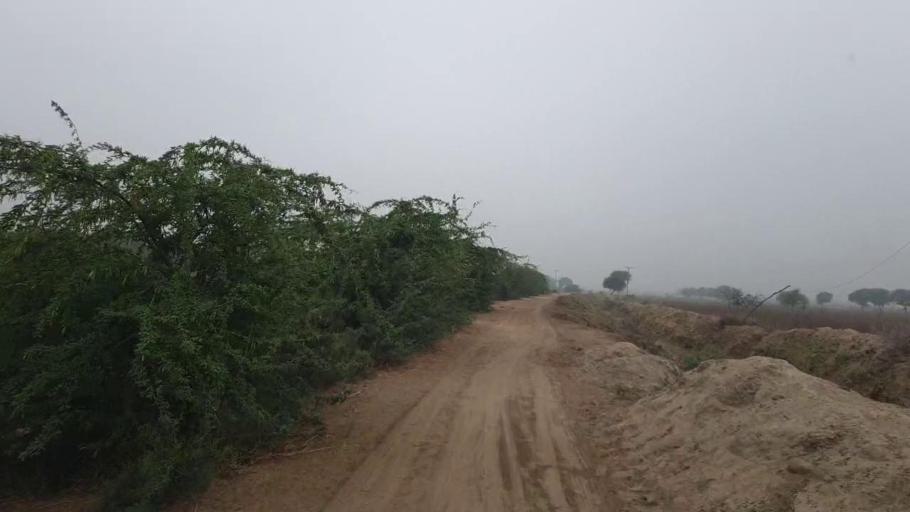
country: PK
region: Sindh
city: Badin
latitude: 24.6311
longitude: 68.6899
